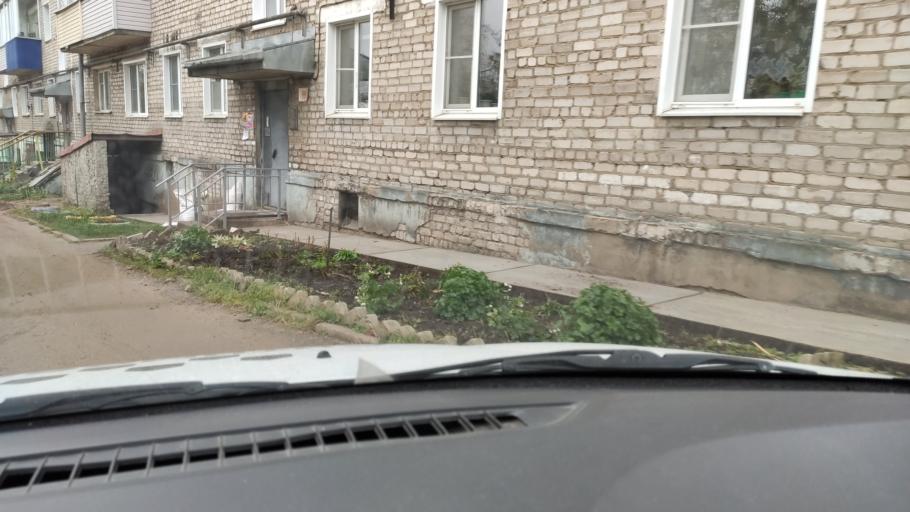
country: RU
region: Kirov
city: Slobodskoy
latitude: 58.7393
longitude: 50.1857
